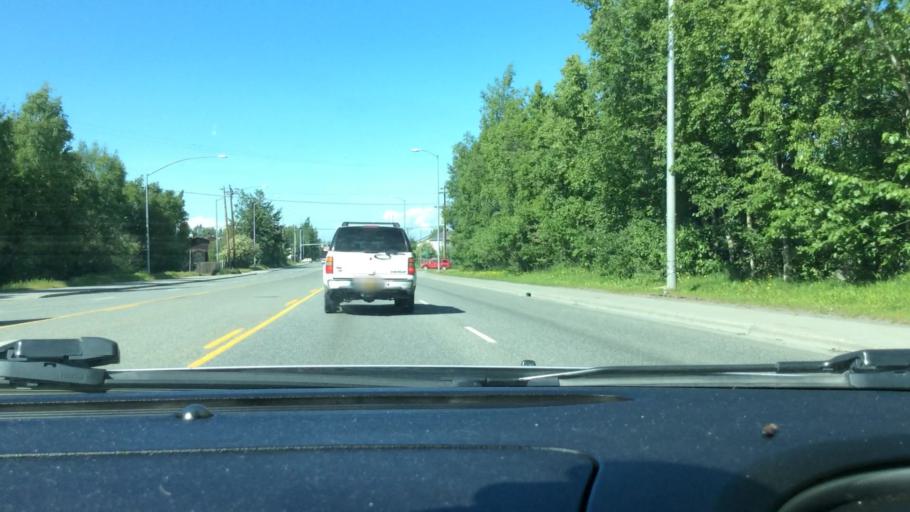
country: US
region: Alaska
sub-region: Anchorage Municipality
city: Anchorage
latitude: 61.2157
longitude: -149.7784
